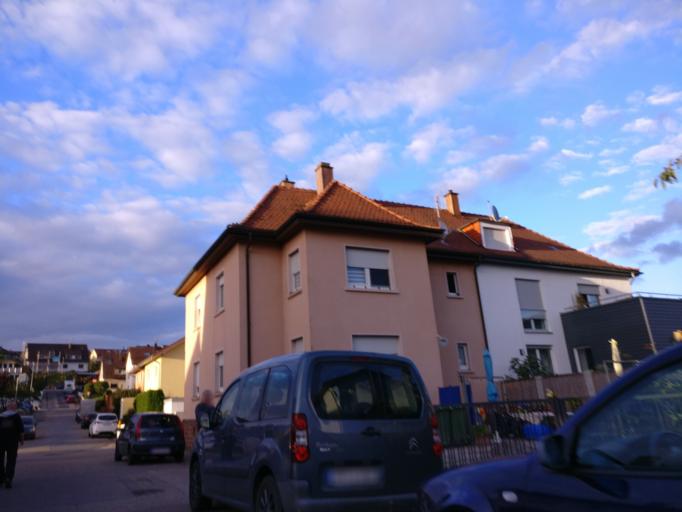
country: DE
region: Baden-Wuerttemberg
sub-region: Karlsruhe Region
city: Konigsbach-Stein
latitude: 48.9655
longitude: 8.6040
